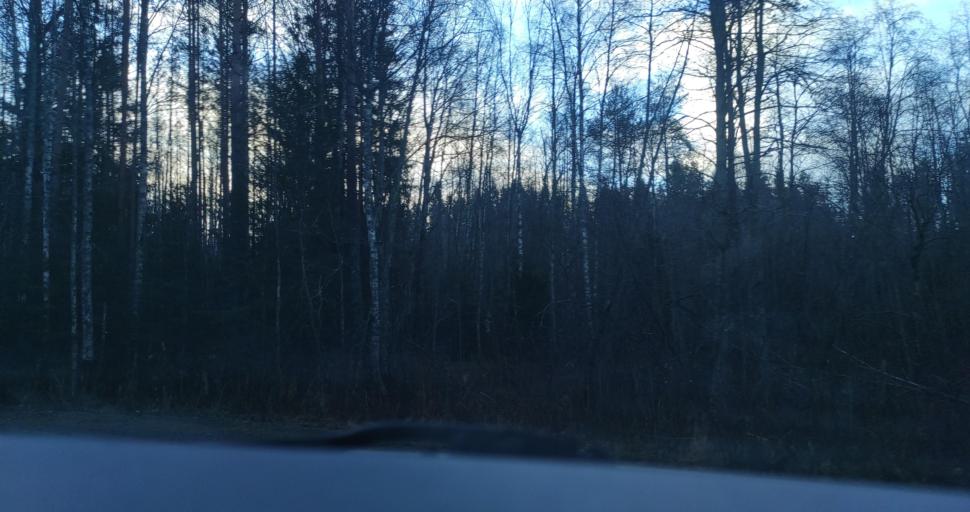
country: RU
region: Republic of Karelia
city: Pitkyaranta
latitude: 61.7333
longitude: 31.3733
